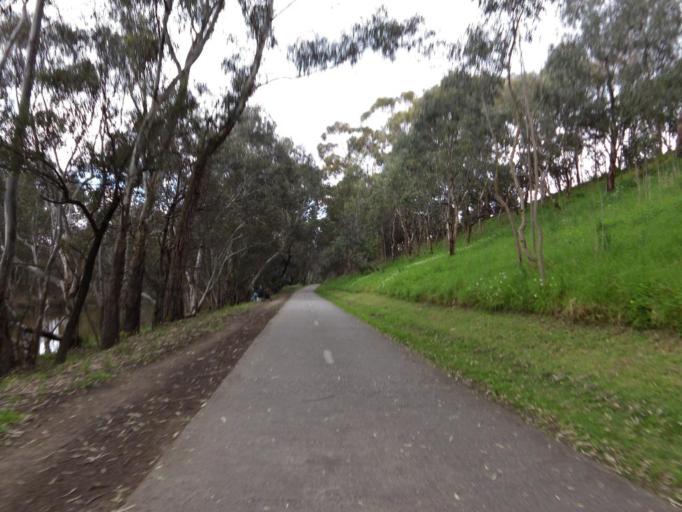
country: AU
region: Victoria
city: Alphington
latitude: -37.7901
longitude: 145.0348
